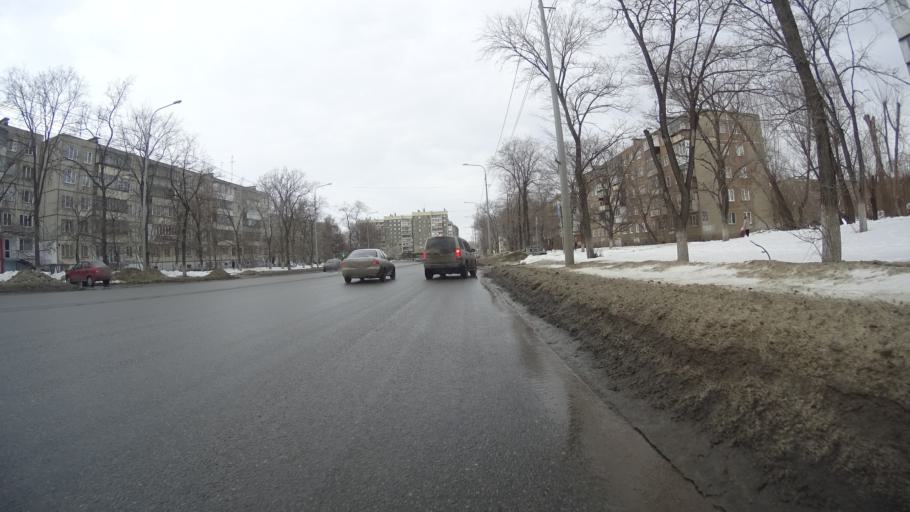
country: RU
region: Chelyabinsk
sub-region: Gorod Chelyabinsk
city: Chelyabinsk
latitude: 55.1964
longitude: 61.3328
